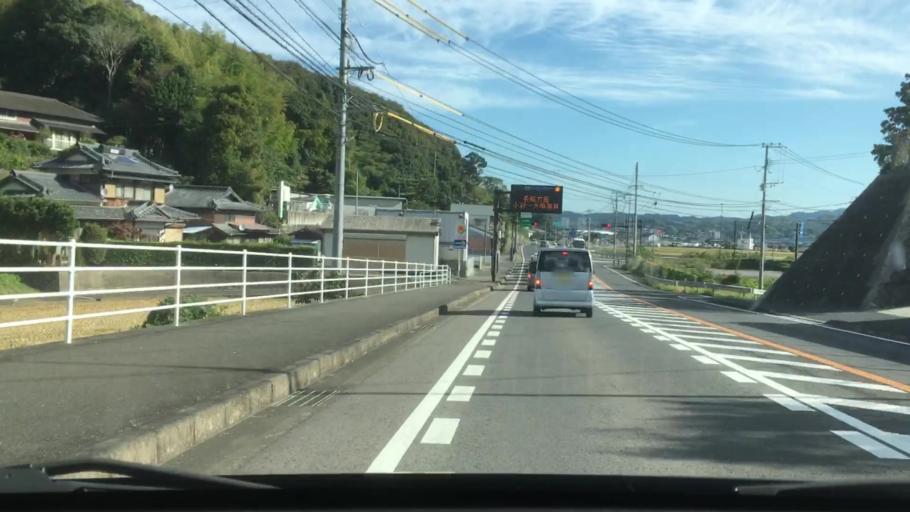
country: JP
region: Nagasaki
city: Sasebo
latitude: 33.1040
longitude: 129.7772
